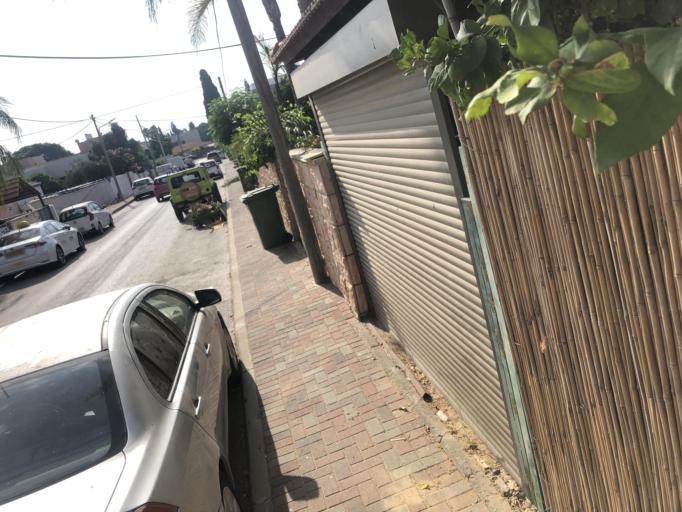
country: IL
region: Central District
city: Yehud
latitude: 32.0390
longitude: 34.8884
